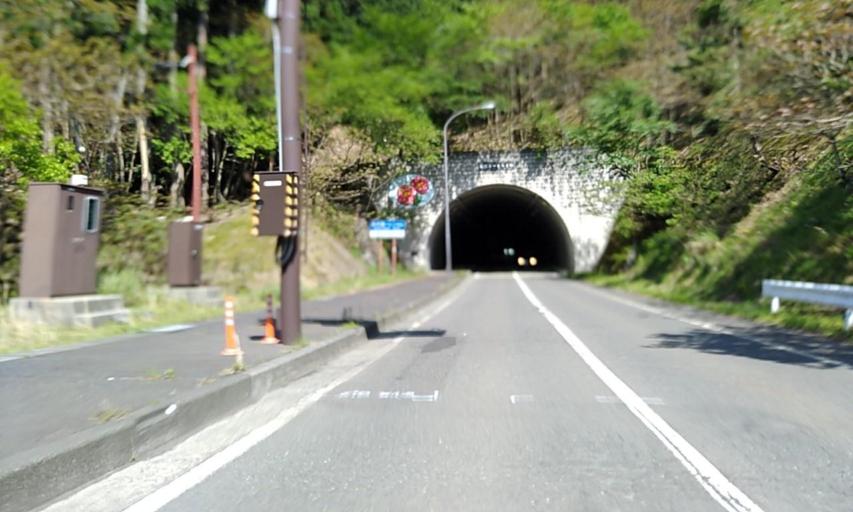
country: JP
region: Fukui
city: Obama
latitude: 35.5259
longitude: 135.8079
